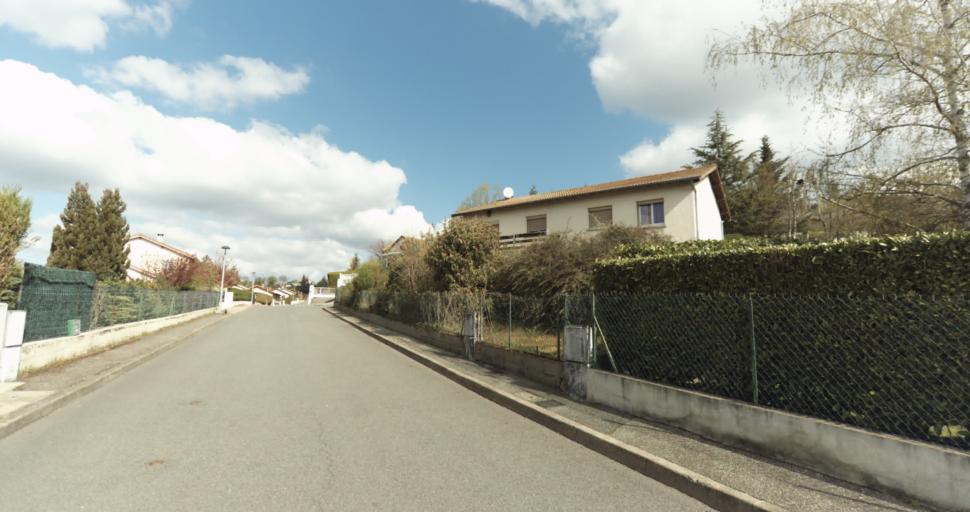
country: FR
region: Rhone-Alpes
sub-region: Departement du Rhone
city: Tarare
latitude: 45.8962
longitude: 4.4469
